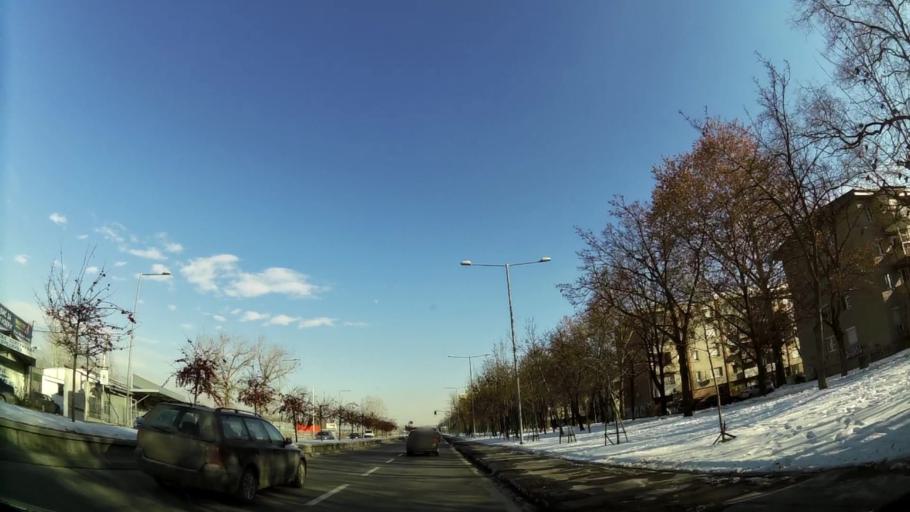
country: MK
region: Karpos
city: Skopje
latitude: 42.0075
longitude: 21.3954
